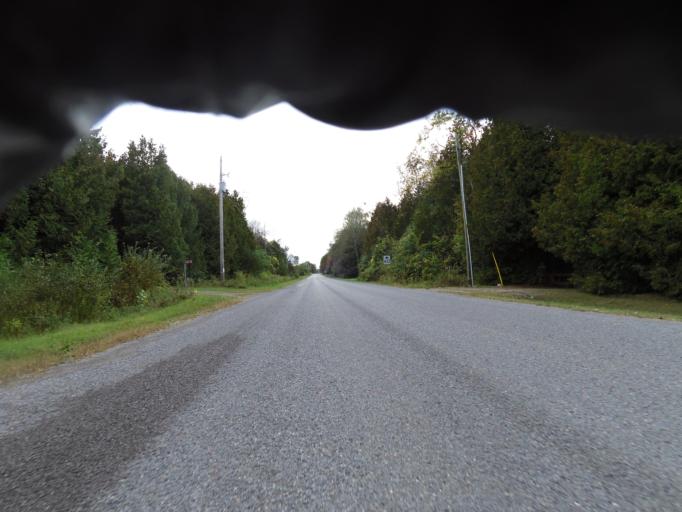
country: CA
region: Ontario
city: Cobourg
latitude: 43.9700
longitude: -78.0450
